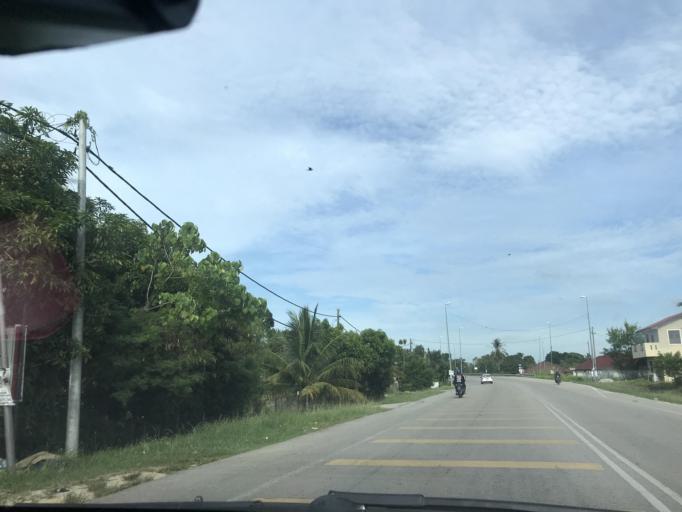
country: MY
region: Kelantan
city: Kota Bharu
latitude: 6.1394
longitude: 102.2039
